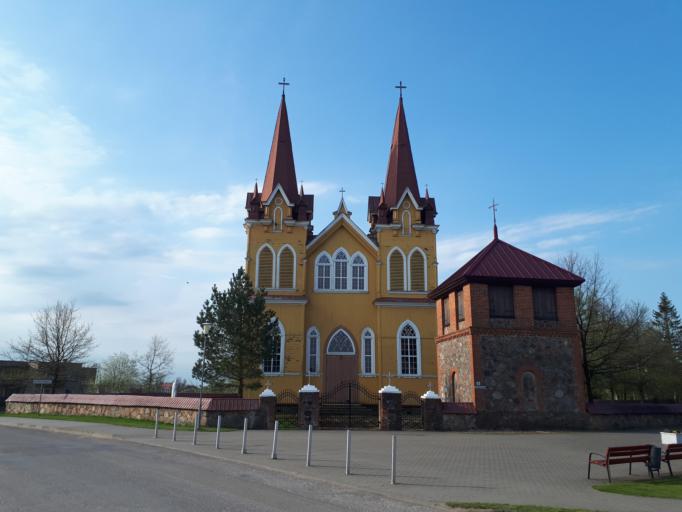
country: LT
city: Rietavas
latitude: 55.8092
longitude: 22.0639
